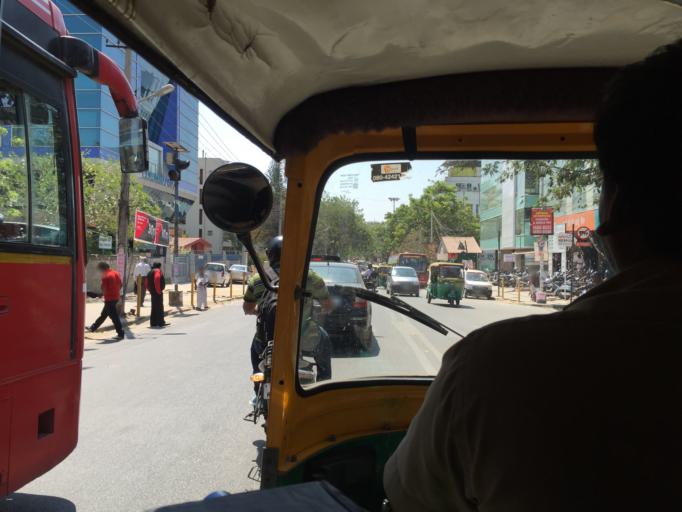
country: IN
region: Karnataka
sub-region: Bangalore Urban
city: Bangalore
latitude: 12.9743
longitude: 77.6469
